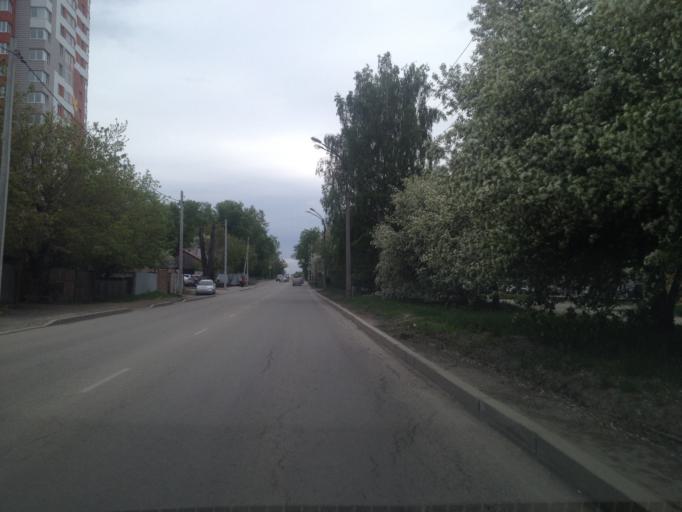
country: RU
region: Sverdlovsk
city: Sovkhoznyy
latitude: 56.7668
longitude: 60.6032
